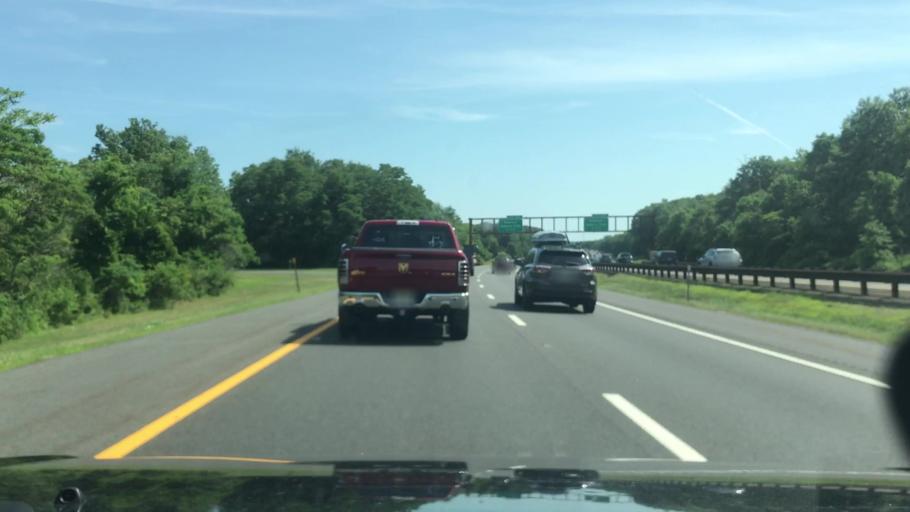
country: US
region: New Jersey
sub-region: Monmouth County
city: Eatontown
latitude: 40.2675
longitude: -74.0786
